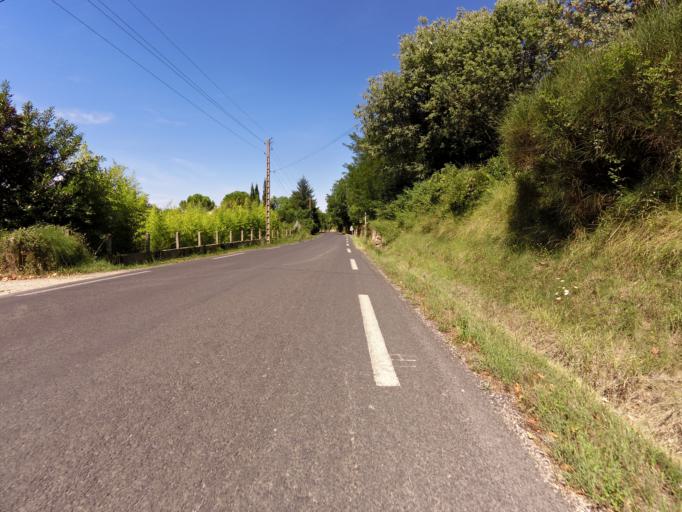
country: FR
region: Languedoc-Roussillon
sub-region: Departement du Gard
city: Sommieres
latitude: 43.7707
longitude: 4.0924
